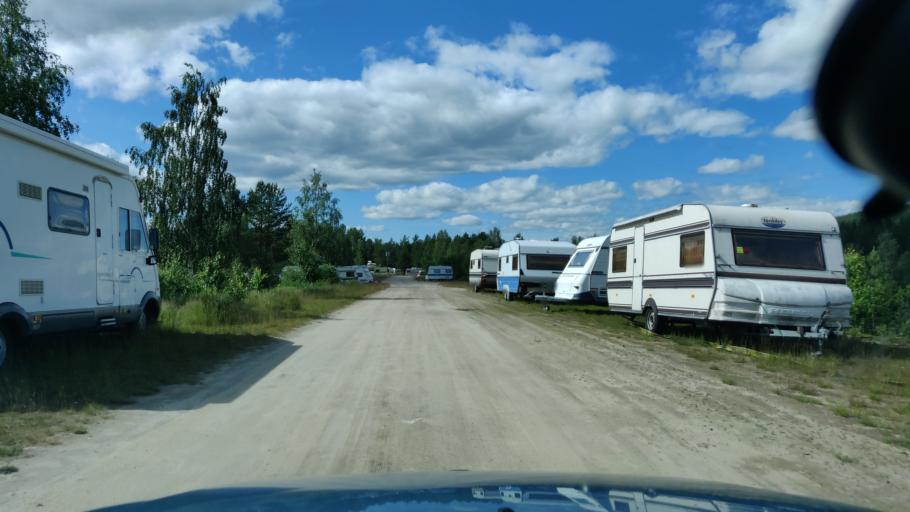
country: NO
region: Hedmark
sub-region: Trysil
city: Innbygda
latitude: 60.9105
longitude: 12.5641
